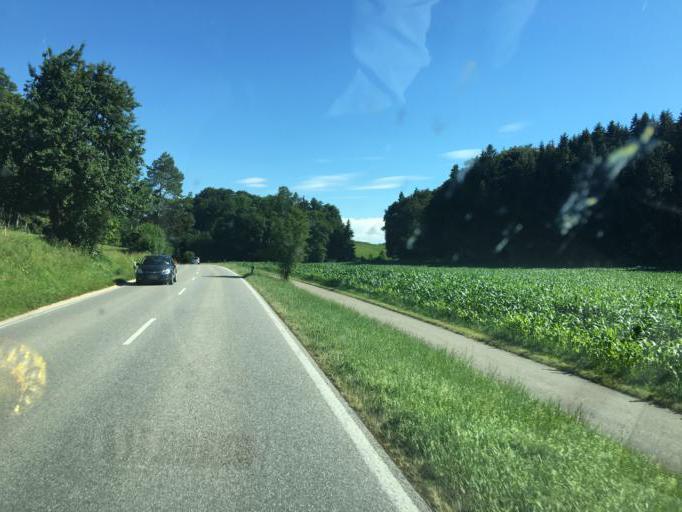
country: DE
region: Bavaria
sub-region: Upper Bavaria
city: Taching am See
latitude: 47.9840
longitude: 12.7301
